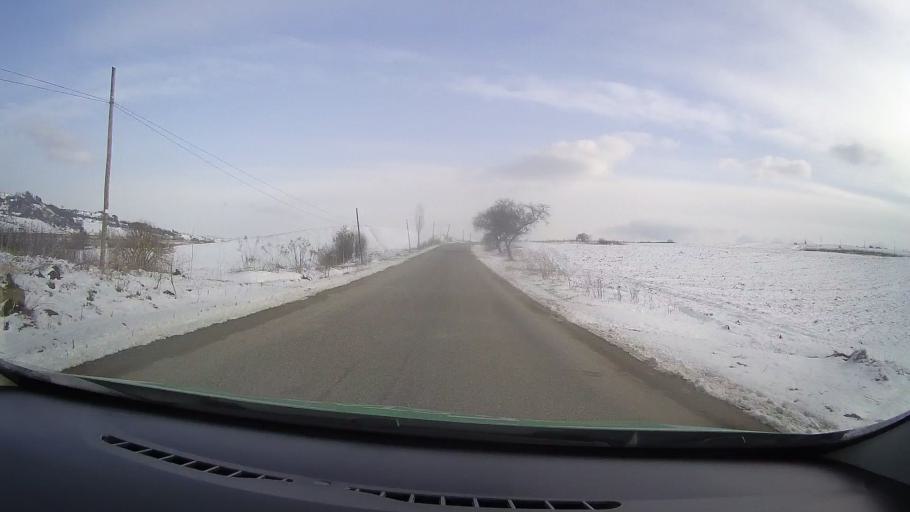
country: RO
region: Sibiu
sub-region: Comuna Merghindeal
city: Merghindeal
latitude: 45.9711
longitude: 24.7080
